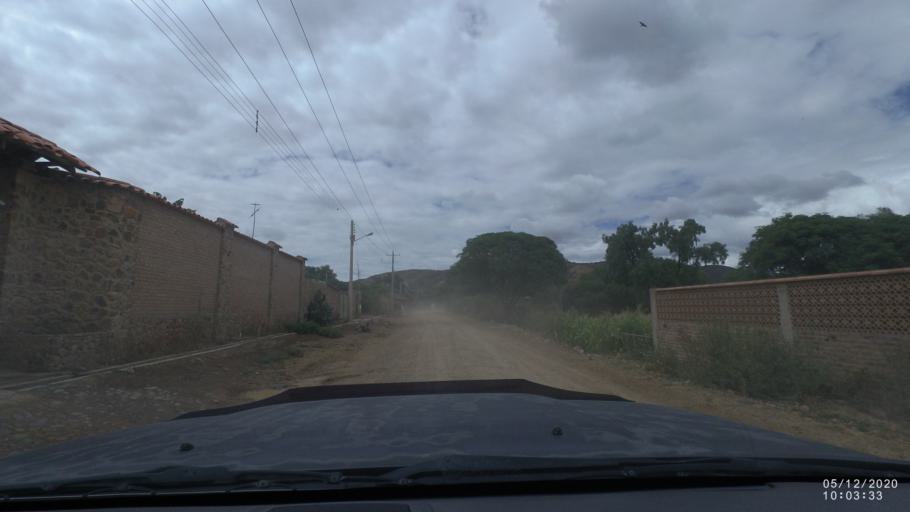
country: BO
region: Cochabamba
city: Sipe Sipe
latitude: -17.4582
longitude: -66.2868
